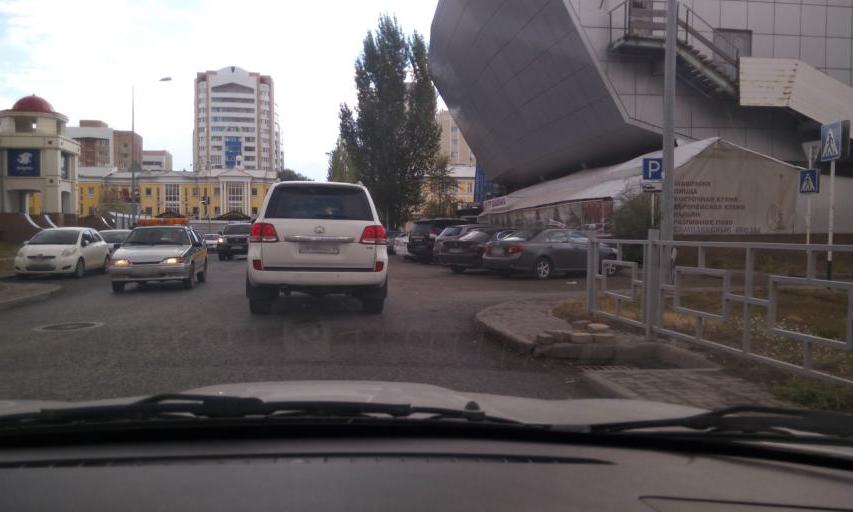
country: KZ
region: Astana Qalasy
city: Astana
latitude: 51.1643
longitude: 71.4319
